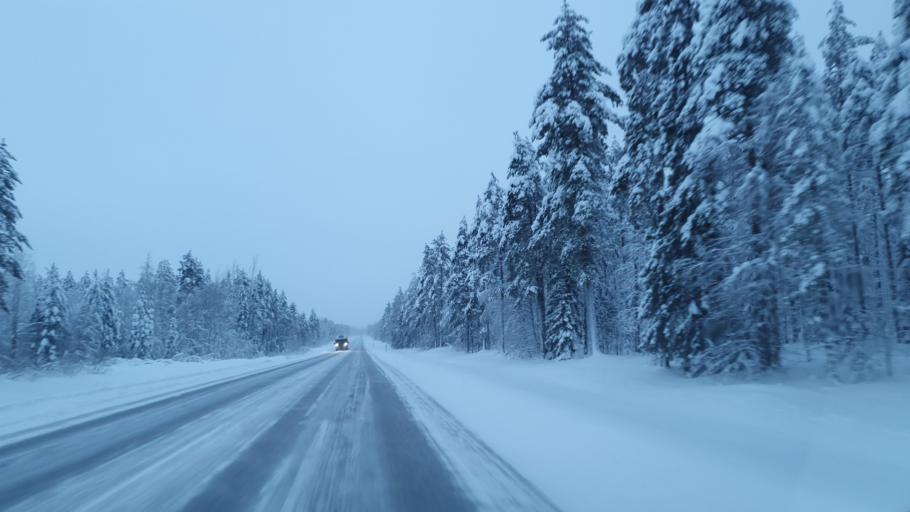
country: FI
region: Kainuu
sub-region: Kajaani
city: Vaala
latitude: 64.5506
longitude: 27.0658
